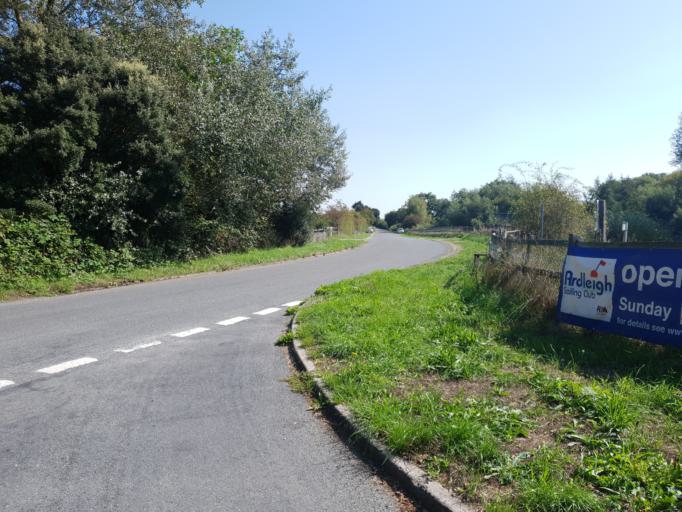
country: GB
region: England
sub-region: Essex
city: Wivenhoe
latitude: 51.9260
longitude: 0.9664
